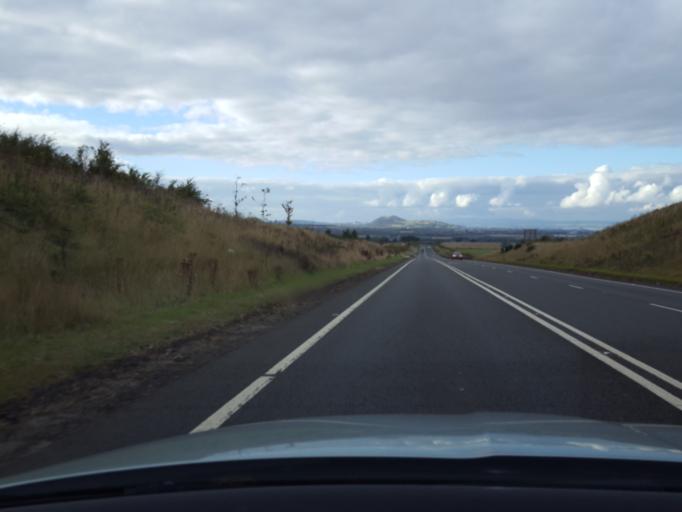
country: GB
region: Scotland
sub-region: Fife
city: Pathhead
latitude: 55.8956
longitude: -3.0077
